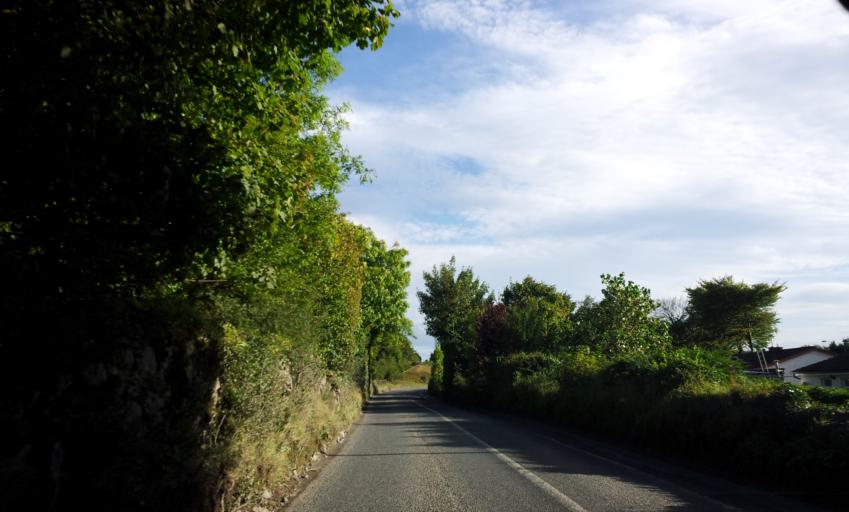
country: IE
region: Munster
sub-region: An Clar
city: Ennis
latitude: 52.8923
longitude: -9.0318
